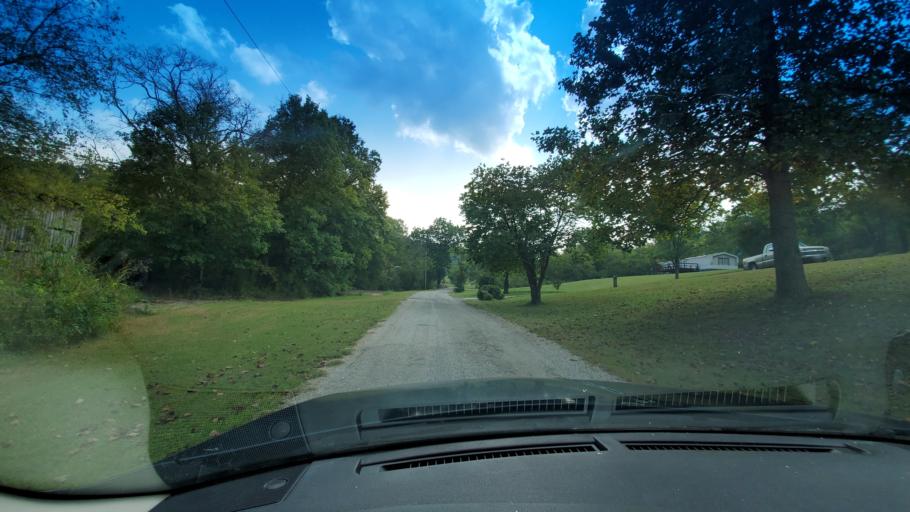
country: US
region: Tennessee
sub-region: Smith County
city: South Carthage
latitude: 36.2285
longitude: -85.9809
